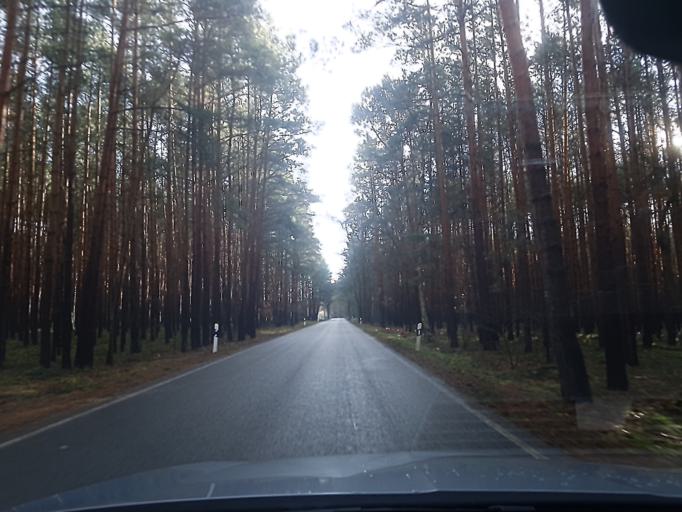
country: DE
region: Brandenburg
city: Schilda
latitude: 51.5691
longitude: 13.3323
